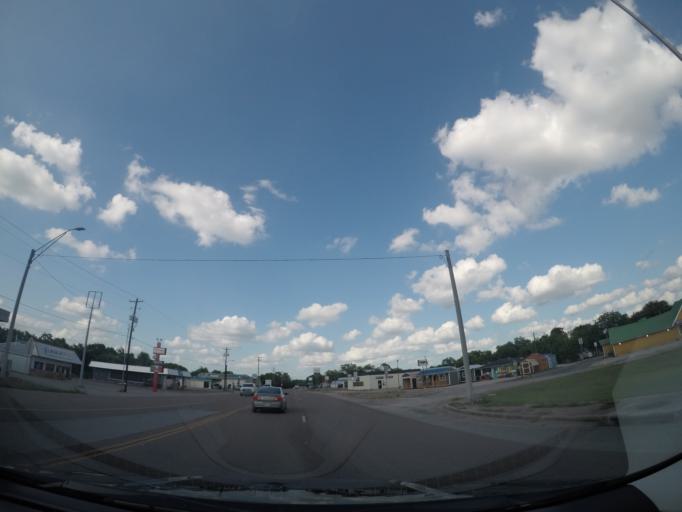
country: US
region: Texas
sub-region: Lavaca County
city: Hallettsville
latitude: 29.4407
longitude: -96.9509
